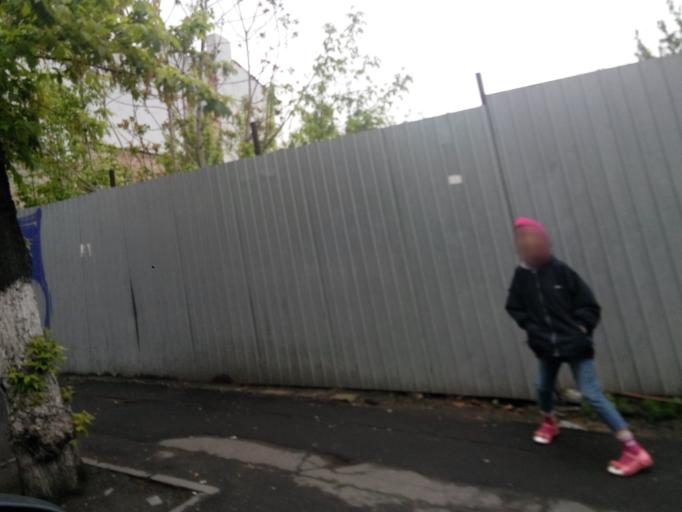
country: RO
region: Bucuresti
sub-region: Municipiul Bucuresti
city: Bucharest
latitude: 44.4375
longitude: 26.1344
